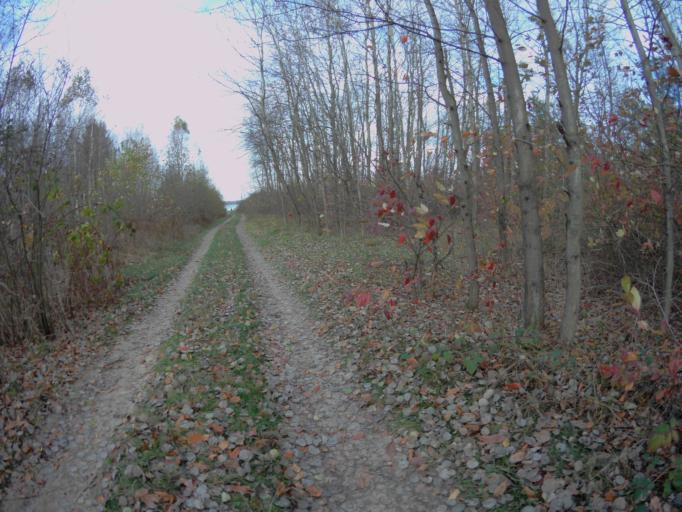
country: PL
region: Subcarpathian Voivodeship
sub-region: Powiat kolbuszowski
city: Lipnica
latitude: 50.3243
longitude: 21.9414
